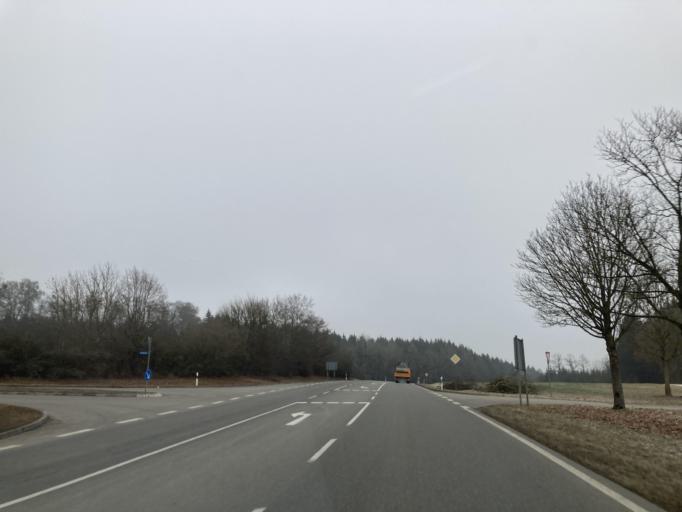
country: DE
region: Baden-Wuerttemberg
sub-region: Freiburg Region
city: Buchheim
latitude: 47.9874
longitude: 9.0058
